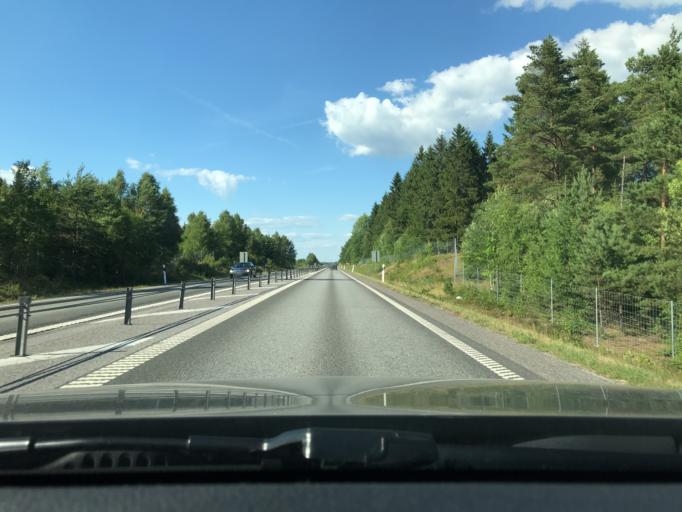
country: SE
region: Kronoberg
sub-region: Almhults Kommun
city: AElmhult
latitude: 56.4877
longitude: 14.1151
